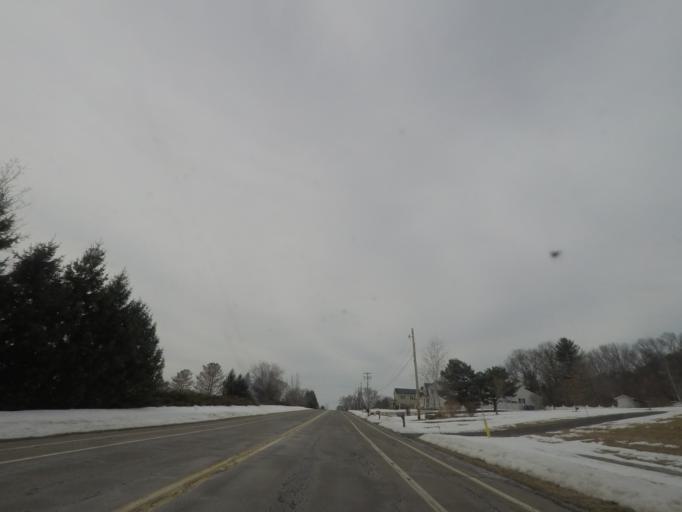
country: US
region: New York
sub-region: Albany County
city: Westmere
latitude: 42.6751
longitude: -73.8919
